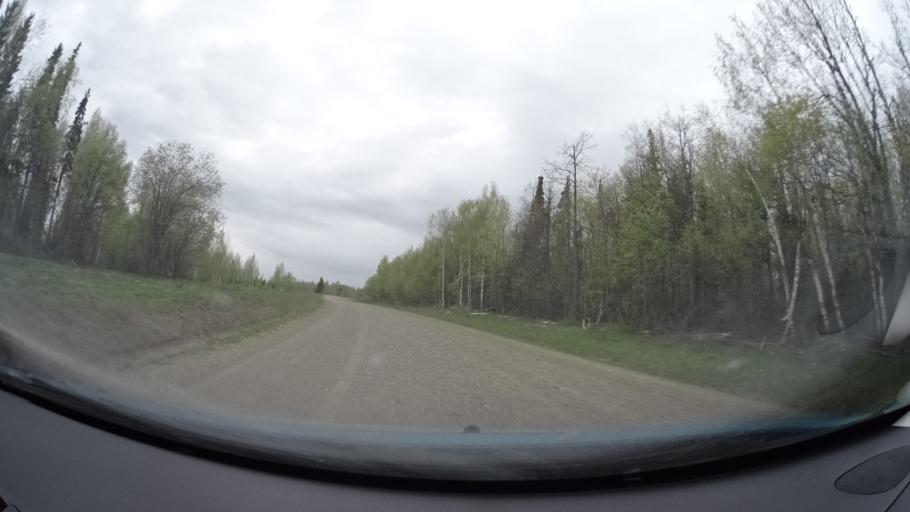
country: RU
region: Perm
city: Kuyeda
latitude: 56.5847
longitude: 55.6905
